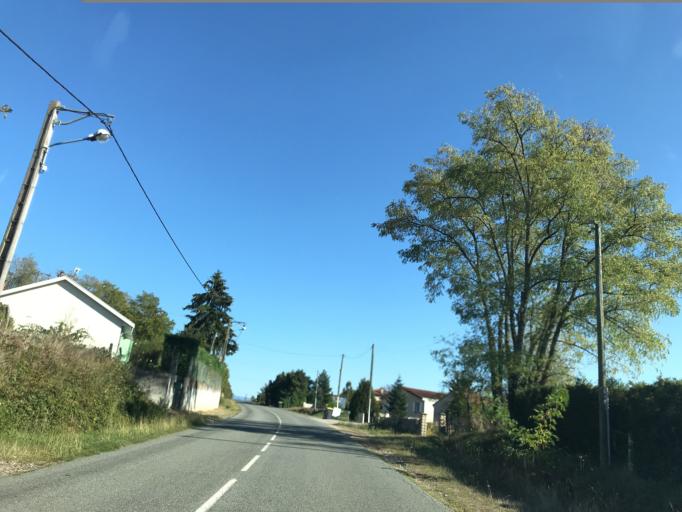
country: FR
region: Auvergne
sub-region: Departement du Puy-de-Dome
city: Lezoux
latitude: 45.7725
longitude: 3.4008
